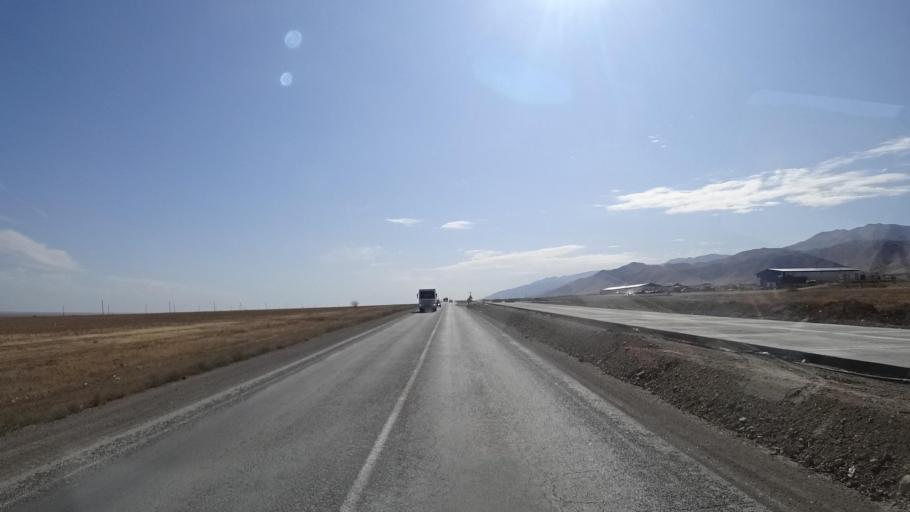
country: KG
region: Chuy
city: Ivanovka
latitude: 43.3912
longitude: 75.1400
